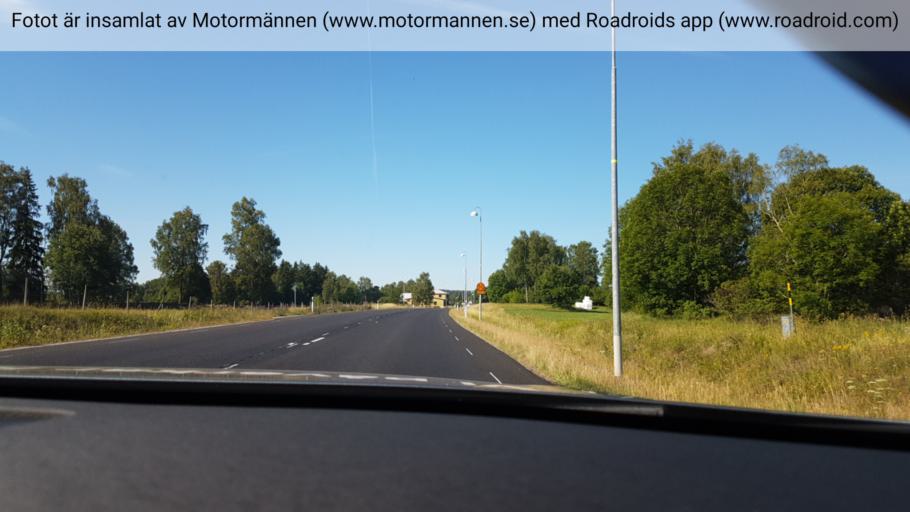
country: SE
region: Vaestra Goetaland
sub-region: Ulricehamns Kommun
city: Ulricehamn
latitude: 57.9382
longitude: 13.5055
